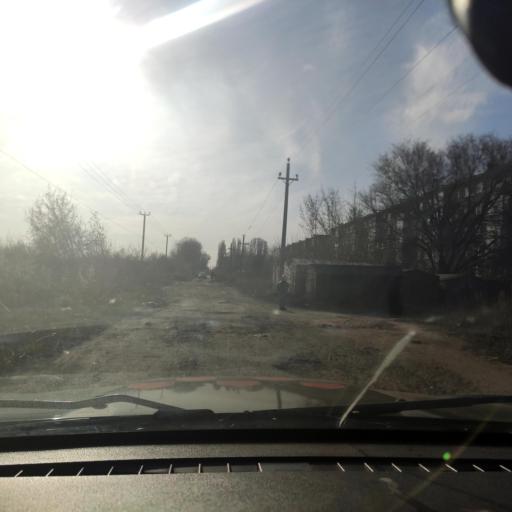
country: RU
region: Samara
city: Tol'yatti
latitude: 53.5666
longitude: 49.3123
